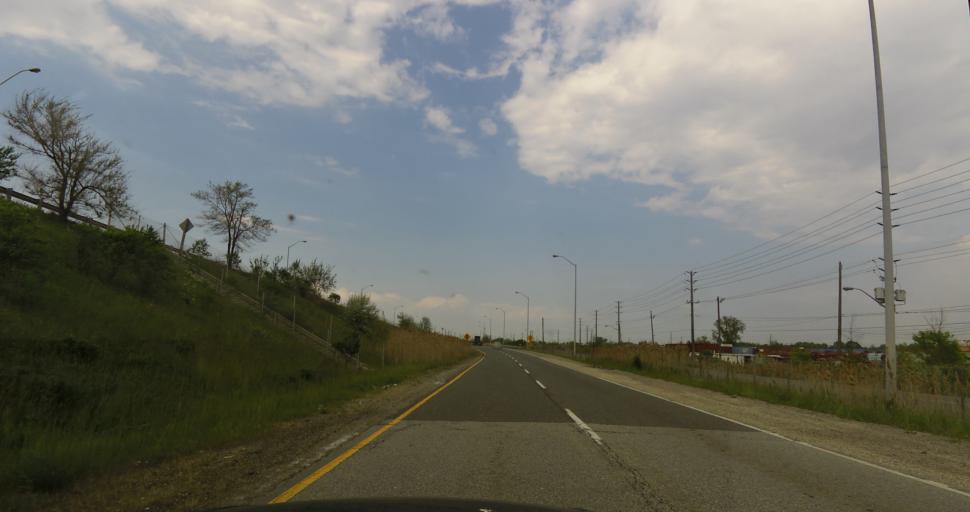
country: CA
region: Ontario
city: Oakville
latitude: 43.4719
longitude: -79.6721
